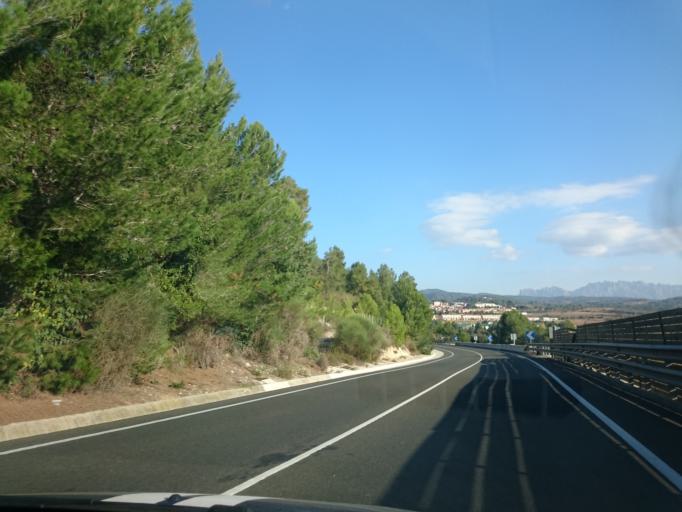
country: ES
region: Catalonia
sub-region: Provincia de Barcelona
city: Capellades
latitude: 41.5072
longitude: 1.7013
